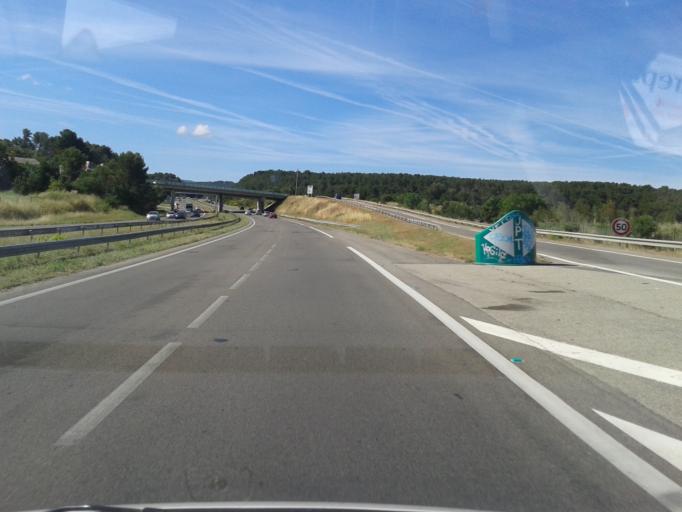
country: FR
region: Provence-Alpes-Cote d'Azur
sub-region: Departement des Bouches-du-Rhone
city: Bouc-Bel-Air
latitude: 43.4738
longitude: 5.4071
